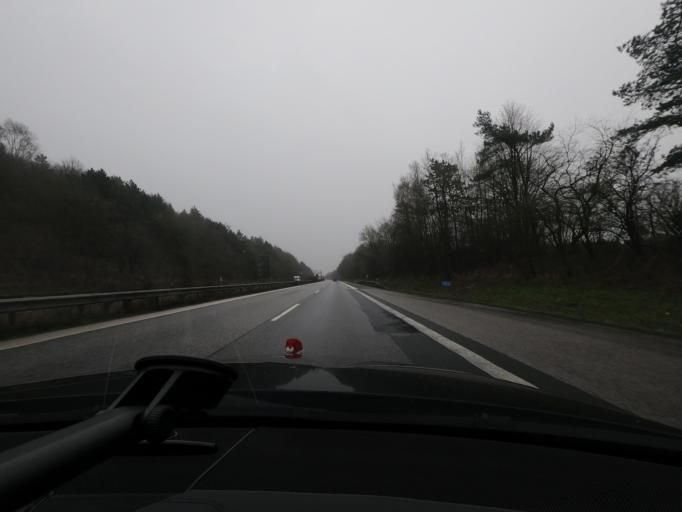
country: DE
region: Schleswig-Holstein
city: Neu Duvenstedt
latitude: 54.3600
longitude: 9.6775
